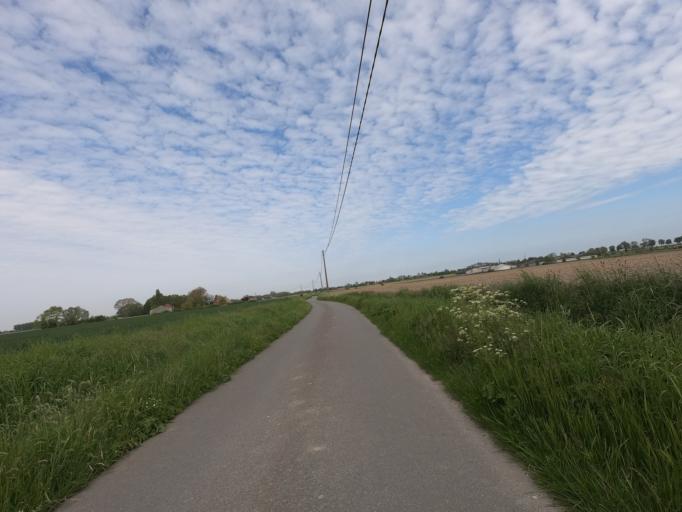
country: BE
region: Flanders
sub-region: Provincie West-Vlaanderen
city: Alveringem
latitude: 50.9656
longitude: 2.7021
